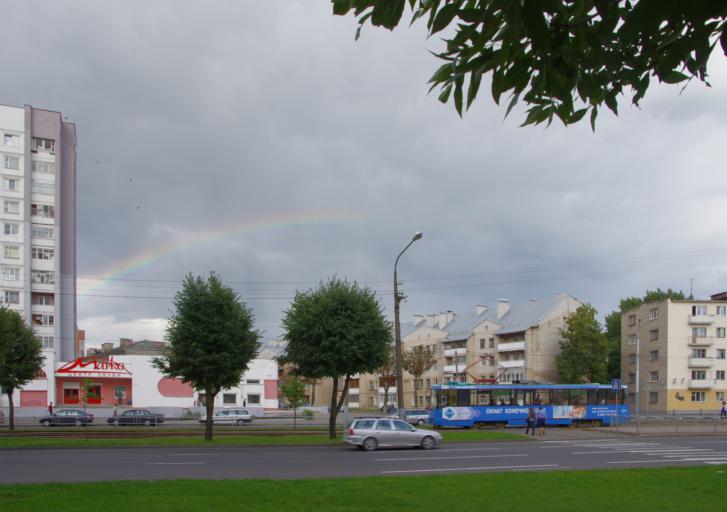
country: BY
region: Vitebsk
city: Vitebsk
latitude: 55.1947
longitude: 30.2282
